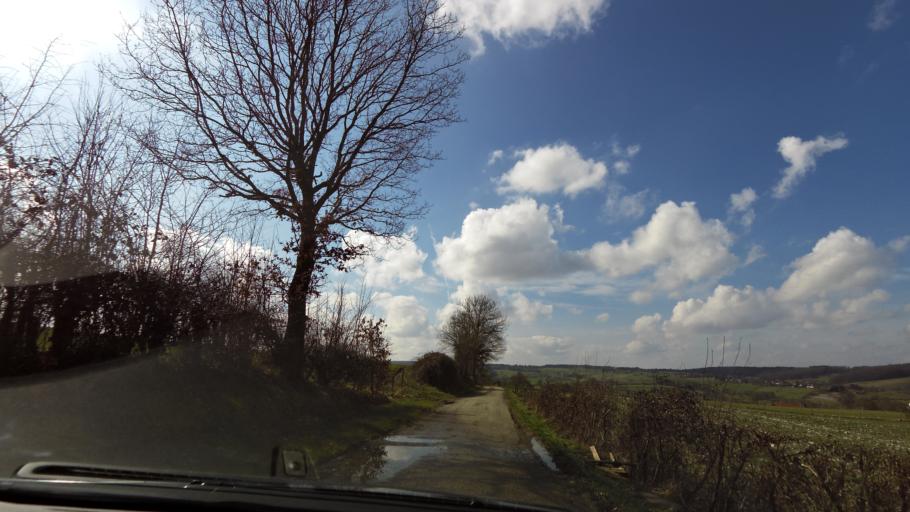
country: BE
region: Wallonia
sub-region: Province de Liege
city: Plombieres
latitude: 50.7857
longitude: 5.9352
